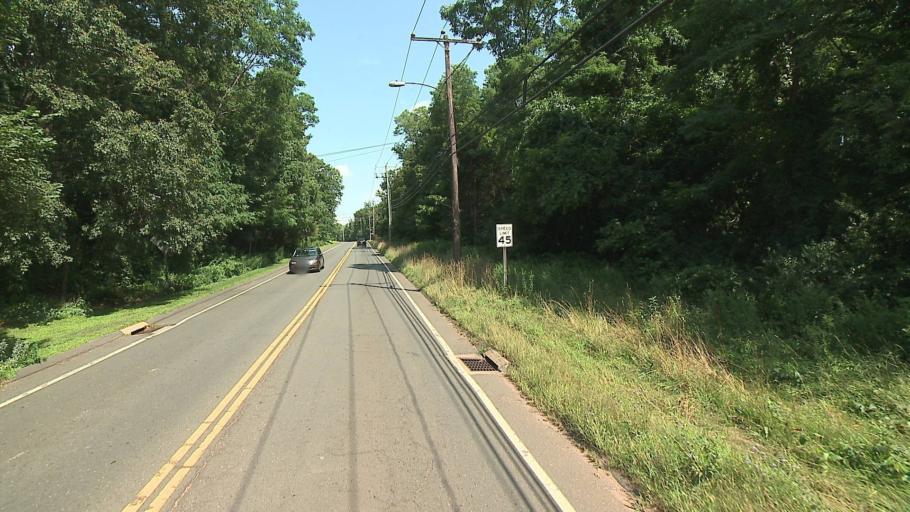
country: US
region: Connecticut
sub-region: Hartford County
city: Plainville
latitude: 41.7081
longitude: -72.8799
